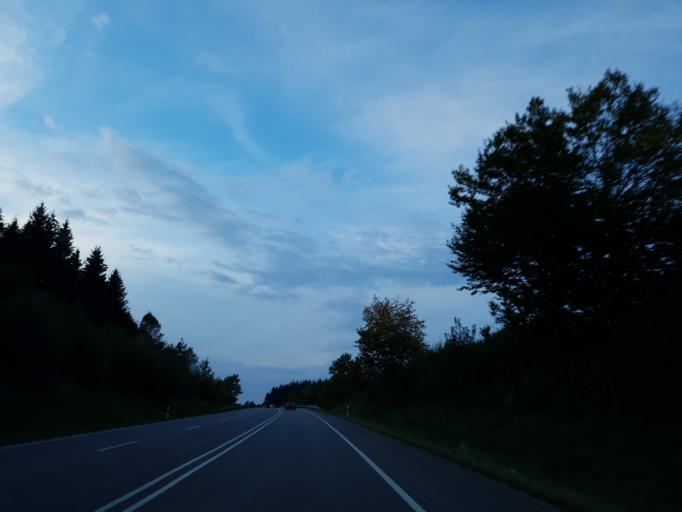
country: DE
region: Bavaria
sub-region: Swabia
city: Biessenhofen
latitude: 47.8417
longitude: 10.6748
